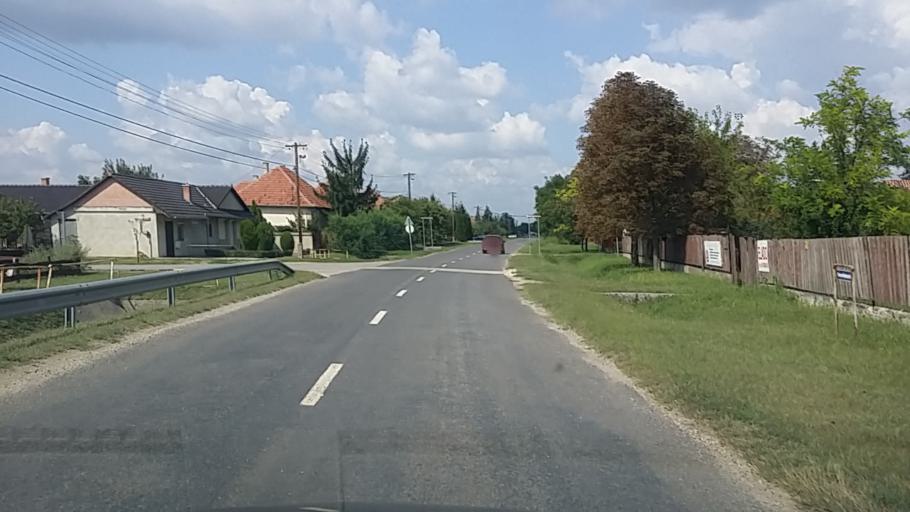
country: HU
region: Bacs-Kiskun
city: Tiszaalpar
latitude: 46.8128
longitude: 20.0002
